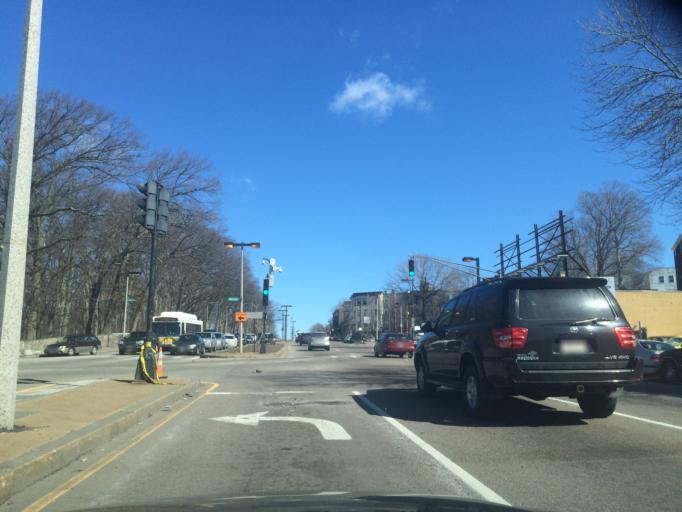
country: US
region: Massachusetts
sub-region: Suffolk County
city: Jamaica Plain
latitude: 42.2979
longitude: -71.0870
